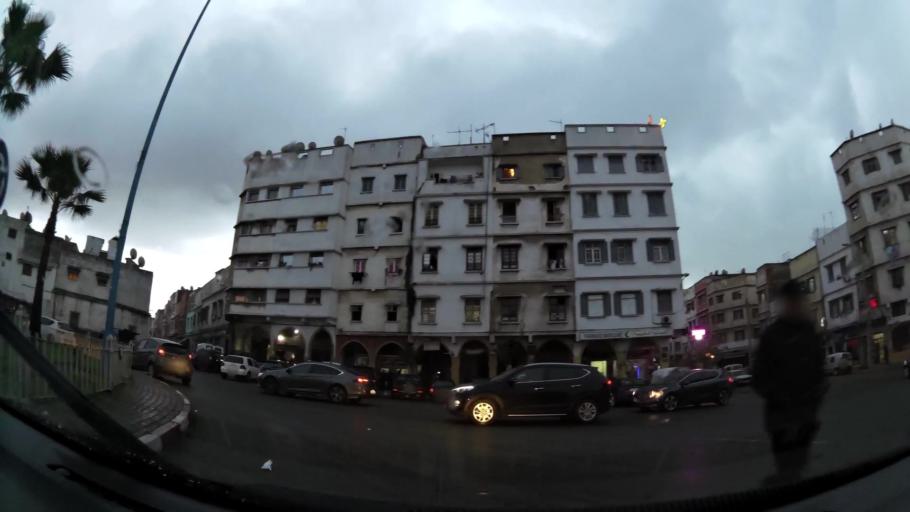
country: MA
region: Grand Casablanca
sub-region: Casablanca
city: Casablanca
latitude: 33.5647
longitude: -7.6044
